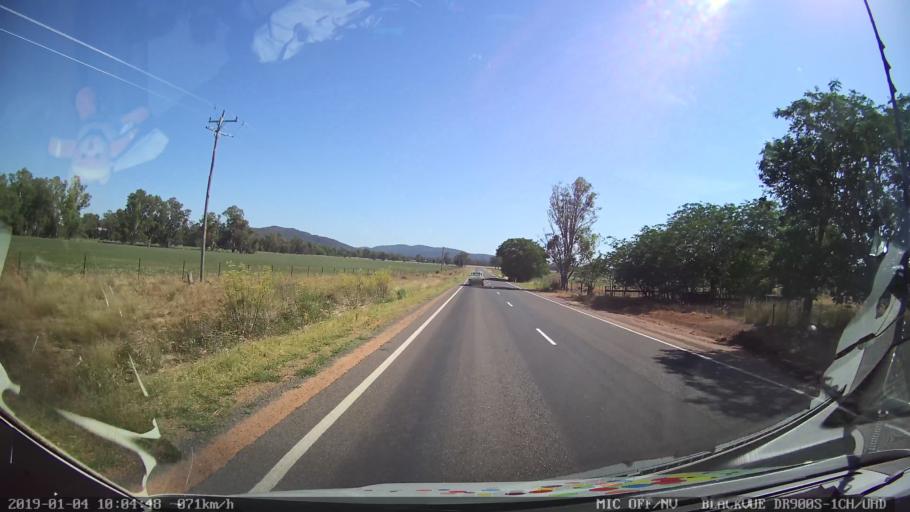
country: AU
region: New South Wales
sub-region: Cabonne
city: Canowindra
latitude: -33.4488
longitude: 148.3626
